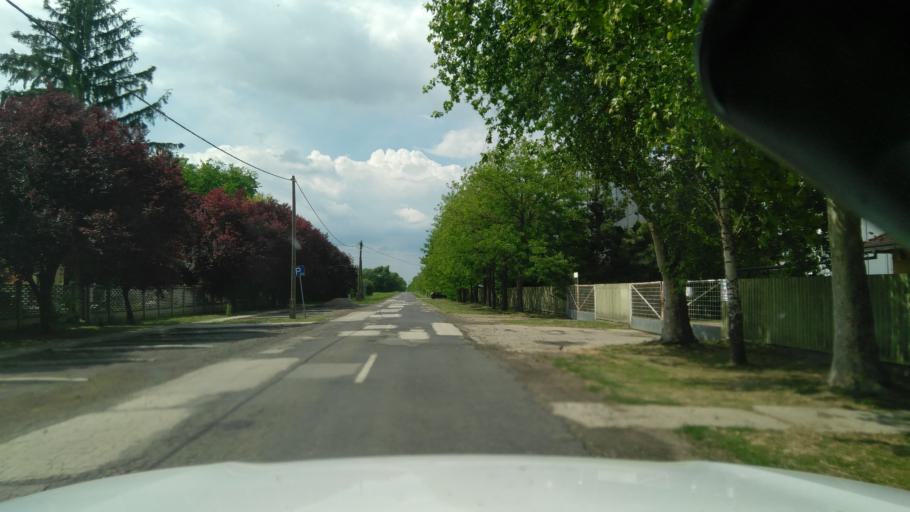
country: HU
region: Bekes
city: Magyarbanhegyes
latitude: 46.4617
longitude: 20.9566
